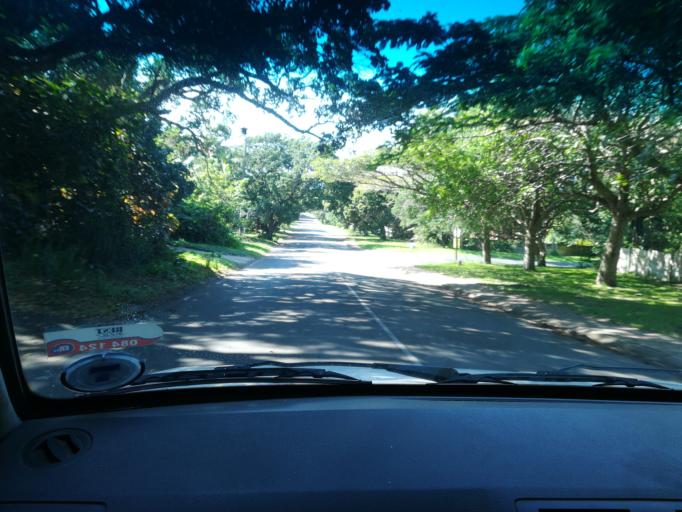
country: ZA
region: KwaZulu-Natal
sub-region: Ugu District Municipality
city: Scottburgh
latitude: -30.3843
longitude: 30.6927
